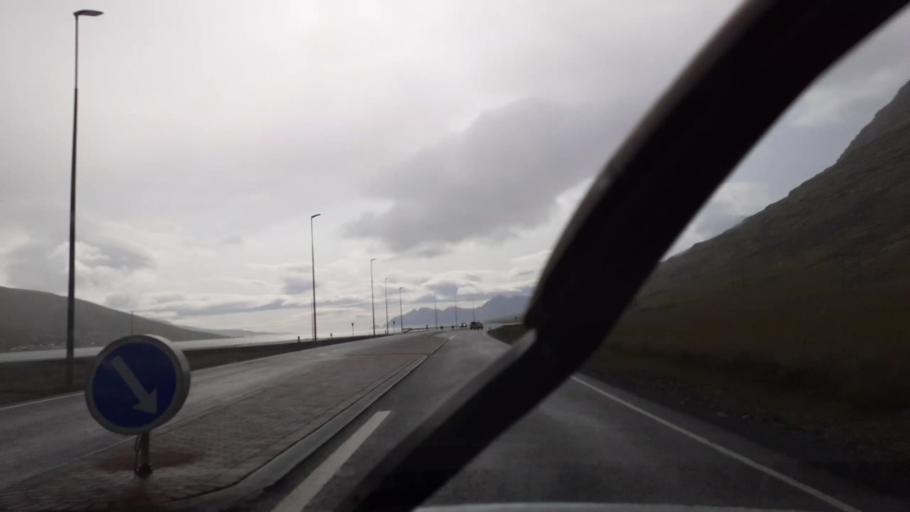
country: IS
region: East
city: Eskifjoerdur
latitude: 65.0744
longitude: -14.0442
